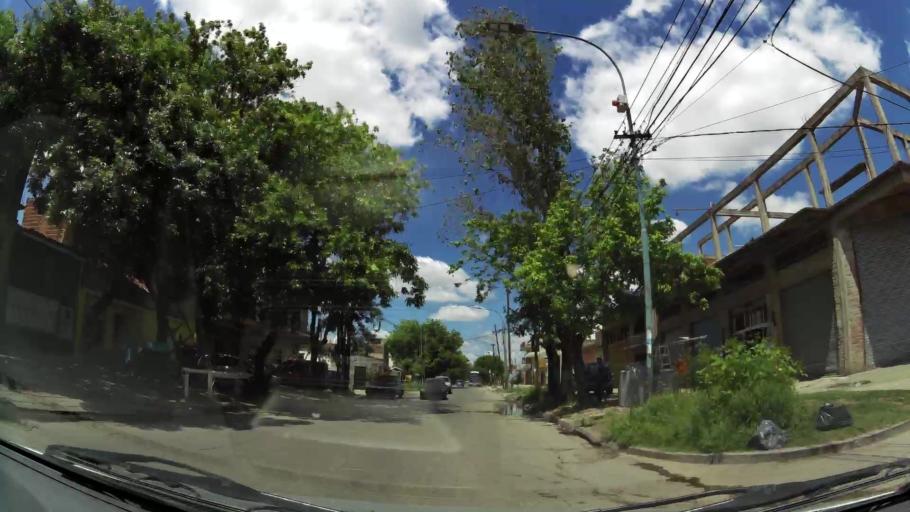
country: AR
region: Buenos Aires
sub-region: Partido de Lanus
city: Lanus
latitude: -34.7172
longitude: -58.4135
